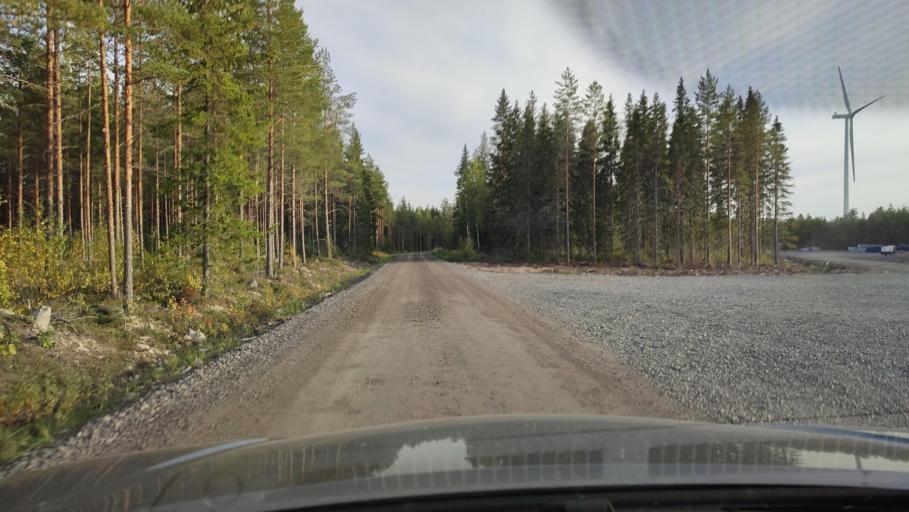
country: FI
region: Southern Ostrobothnia
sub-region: Suupohja
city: Karijoki
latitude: 62.1616
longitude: 21.6108
